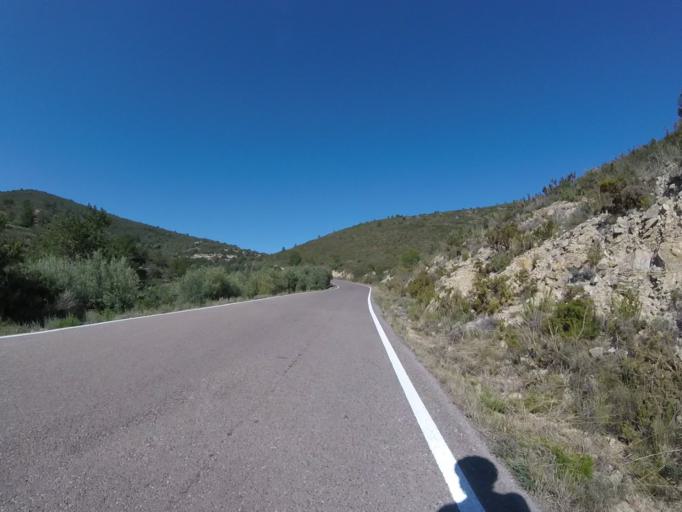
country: ES
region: Valencia
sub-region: Provincia de Castello
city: Santa Magdalena de Pulpis
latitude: 40.3846
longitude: 0.2584
